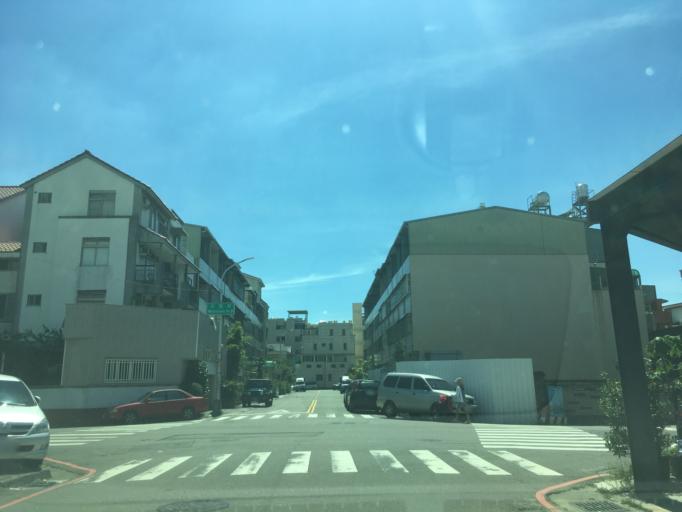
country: TW
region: Taiwan
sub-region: Taichung City
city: Taichung
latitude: 24.1456
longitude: 120.7080
